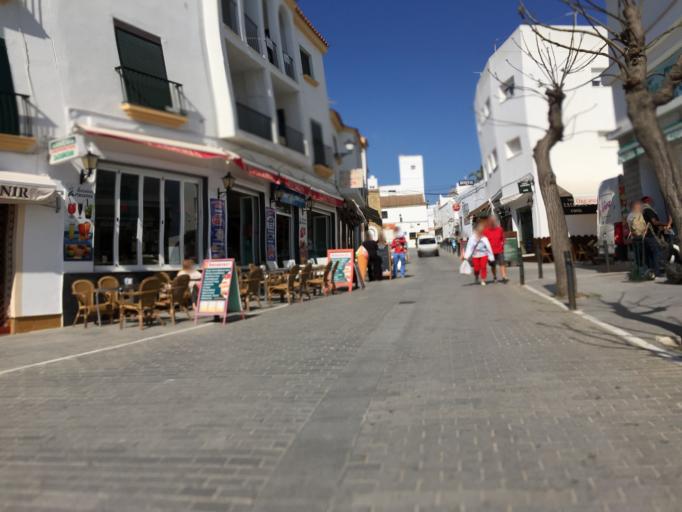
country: ES
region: Andalusia
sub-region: Provincia de Cadiz
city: Conil de la Frontera
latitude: 36.2740
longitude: -6.0899
